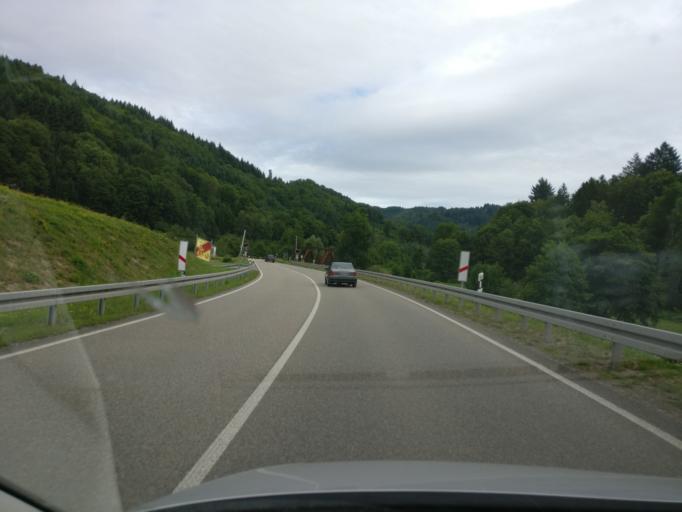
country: DE
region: Baden-Wuerttemberg
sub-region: Freiburg Region
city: Lautenbach
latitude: 48.5155
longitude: 8.1213
